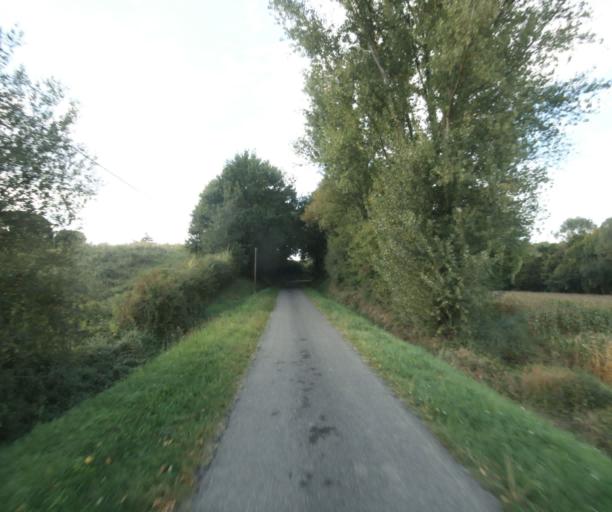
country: FR
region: Midi-Pyrenees
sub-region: Departement du Gers
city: Le Houga
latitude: 43.8420
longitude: -0.1317
